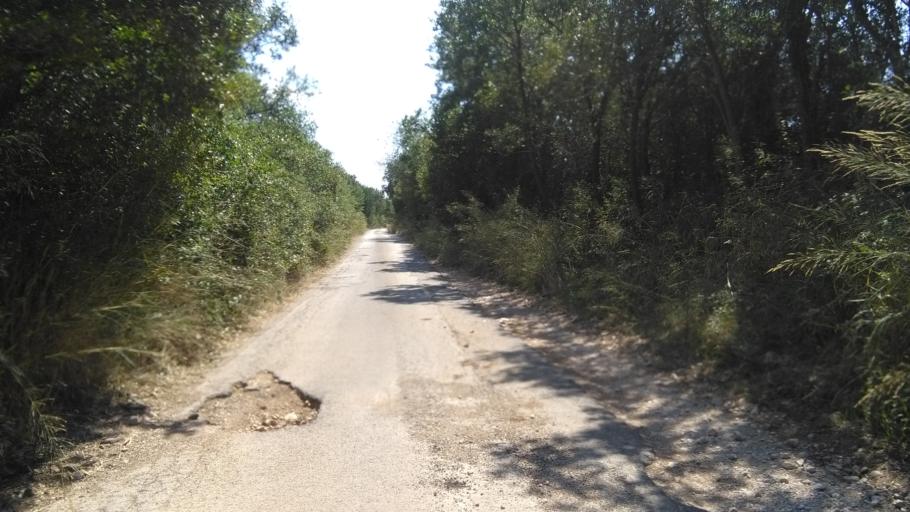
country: IT
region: Apulia
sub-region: Provincia di Bari
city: Noci
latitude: 40.8129
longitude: 17.1801
